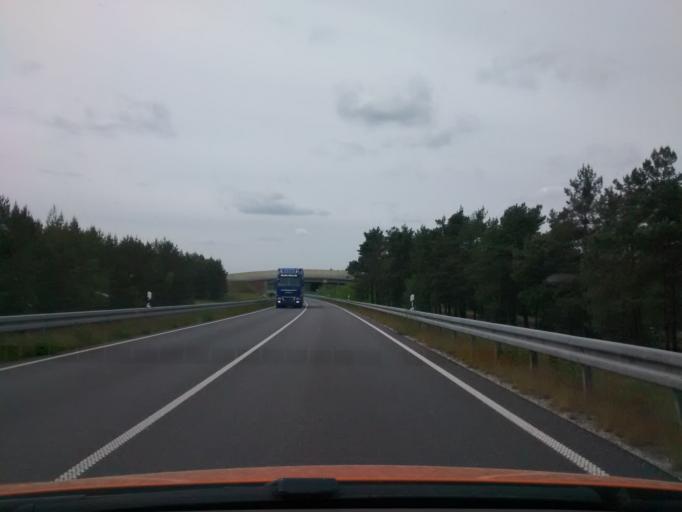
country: DE
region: Brandenburg
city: Luckenwalde
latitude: 52.0681
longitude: 13.1238
